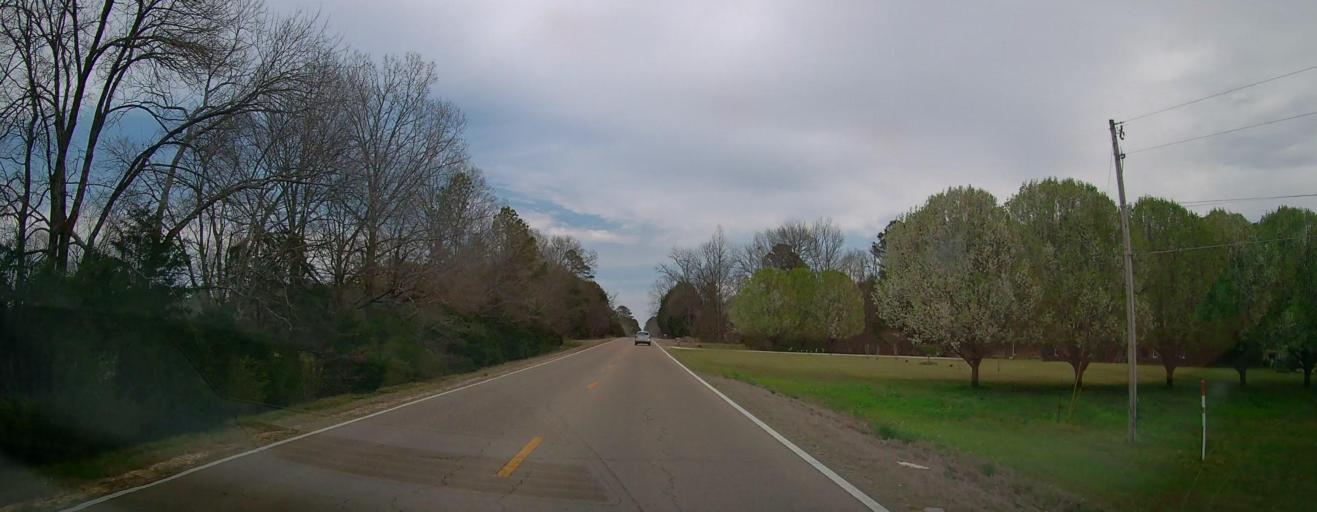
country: US
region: Mississippi
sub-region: Lee County
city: Plantersville
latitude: 34.2662
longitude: -88.6031
